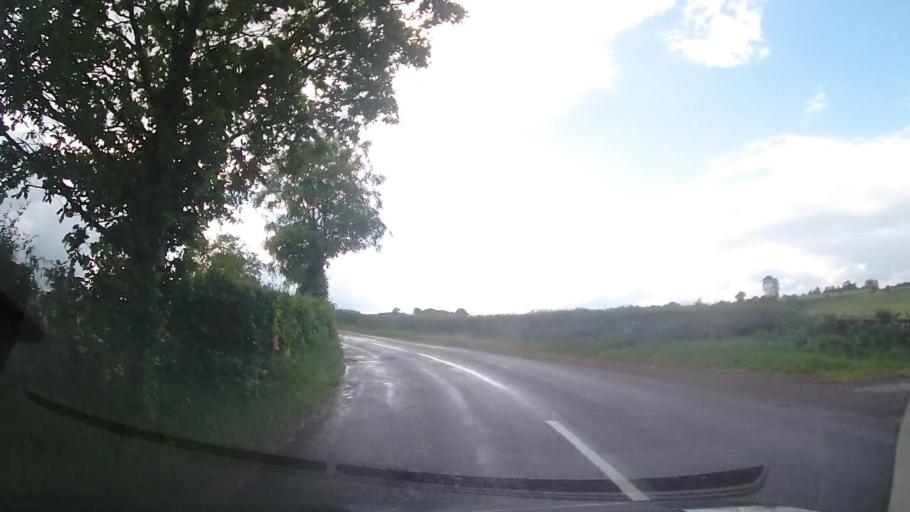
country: GB
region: England
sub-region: Telford and Wrekin
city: Ironbridge
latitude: 52.6600
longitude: -2.5096
